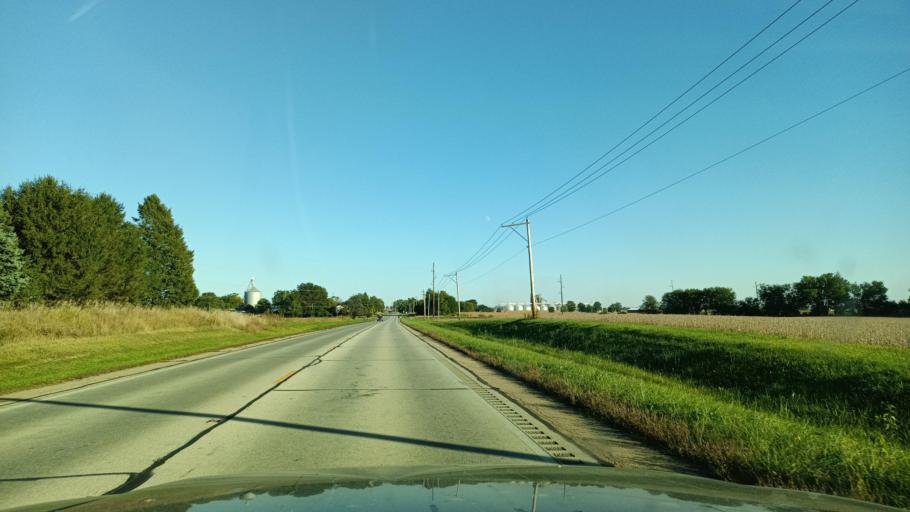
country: US
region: Illinois
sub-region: Champaign County
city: Lake of the Woods
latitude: 40.1732
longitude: -88.3416
